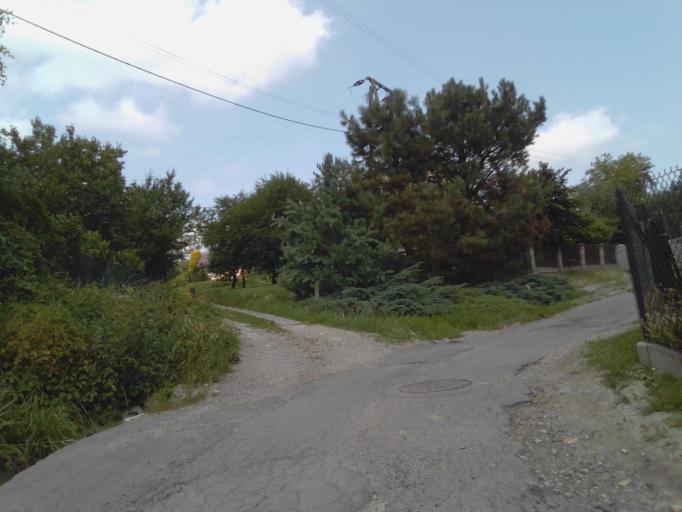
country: PL
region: Subcarpathian Voivodeship
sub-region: Powiat strzyzowski
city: Czudec
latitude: 49.9464
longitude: 21.8367
